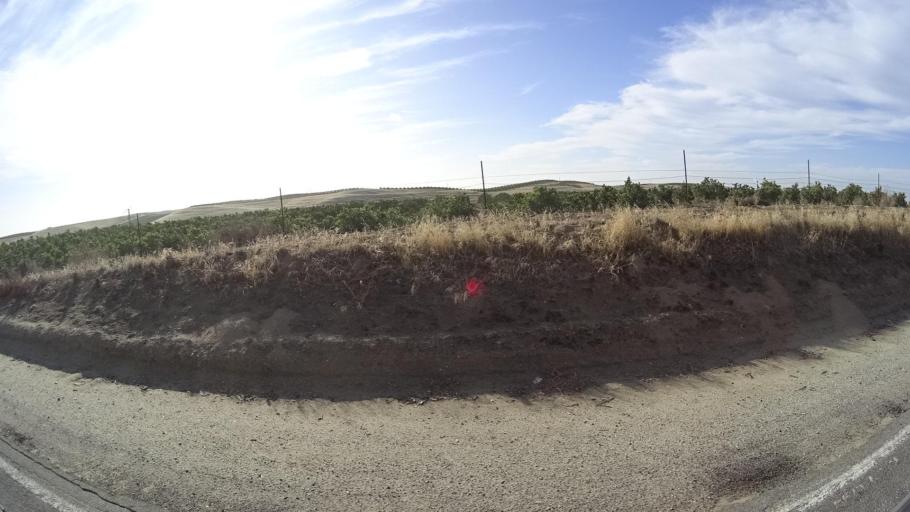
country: US
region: California
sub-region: Kern County
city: McFarland
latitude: 35.6025
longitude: -119.0736
